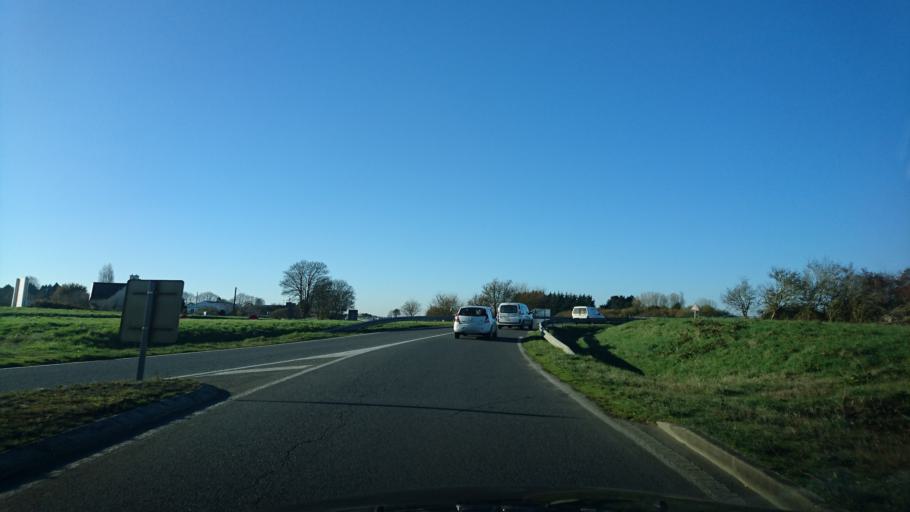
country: FR
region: Brittany
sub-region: Departement des Cotes-d'Armor
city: Tremuson
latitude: 48.5225
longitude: -2.8725
